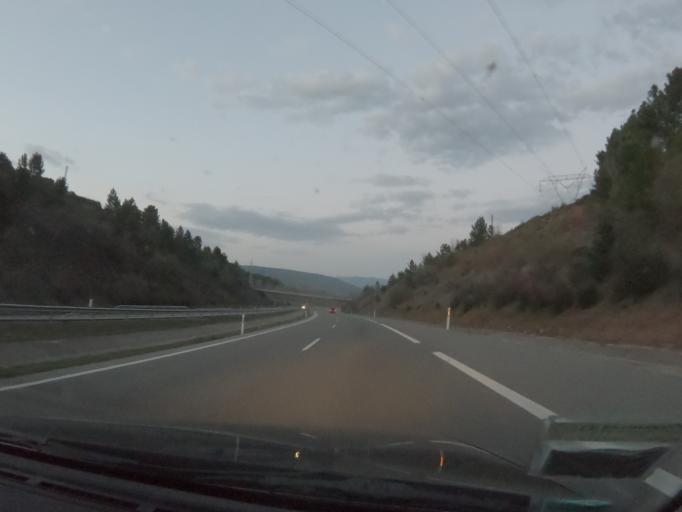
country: ES
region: Castille and Leon
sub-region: Provincia de Leon
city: Molinaseca
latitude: 42.5719
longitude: -6.5371
